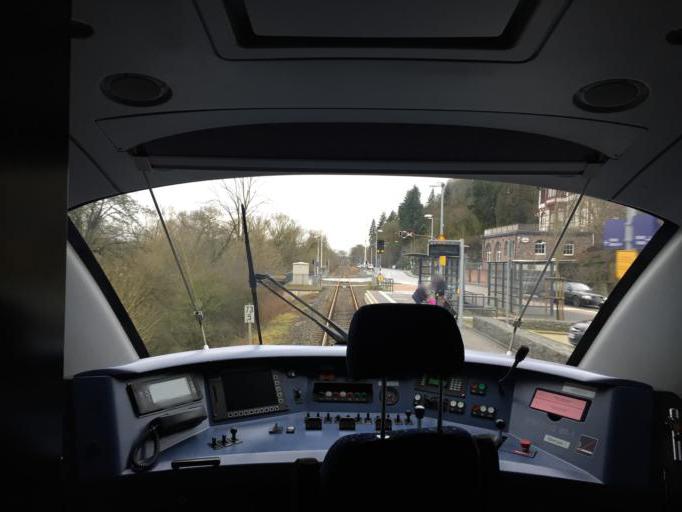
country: DE
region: Hesse
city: Frankenberg
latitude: 51.0653
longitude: 8.7998
